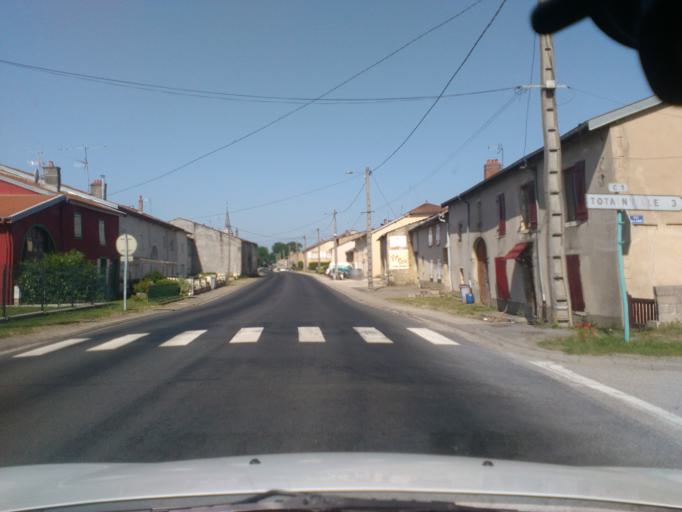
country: FR
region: Lorraine
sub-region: Departement des Vosges
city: Mirecourt
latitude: 48.3105
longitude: 6.0157
